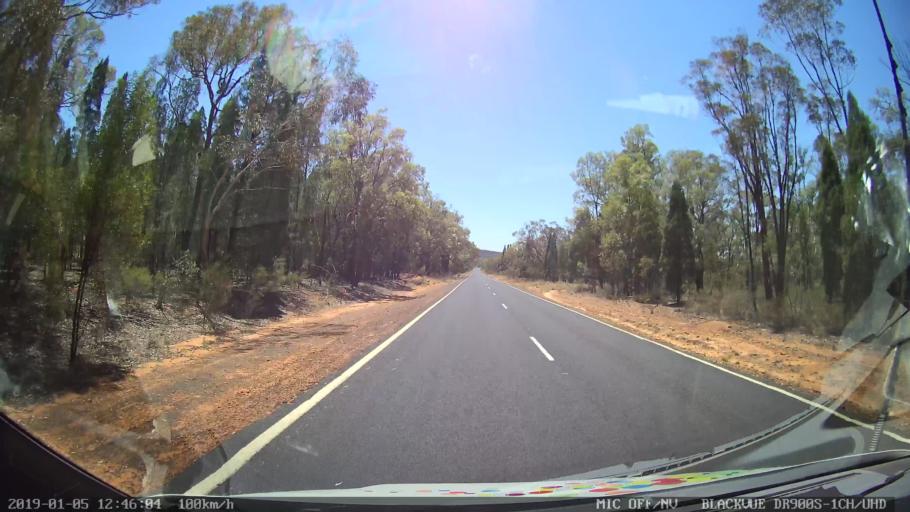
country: AU
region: New South Wales
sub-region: Warrumbungle Shire
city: Coonabarabran
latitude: -31.1217
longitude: 149.5578
